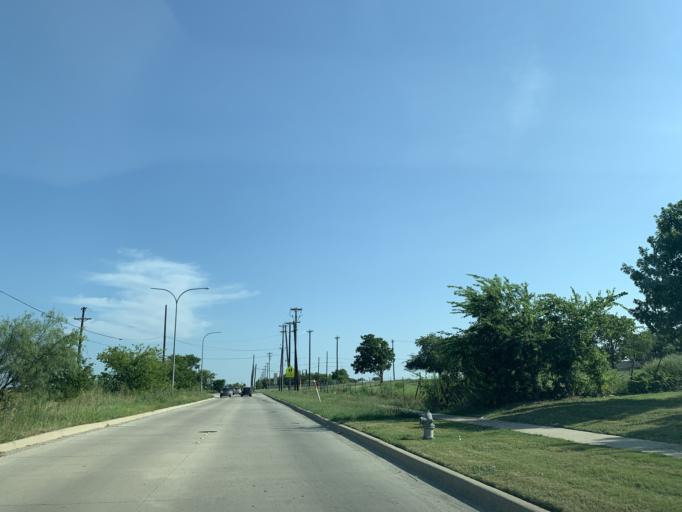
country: US
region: Texas
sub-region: Tarrant County
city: Blue Mound
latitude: 32.8892
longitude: -97.3069
